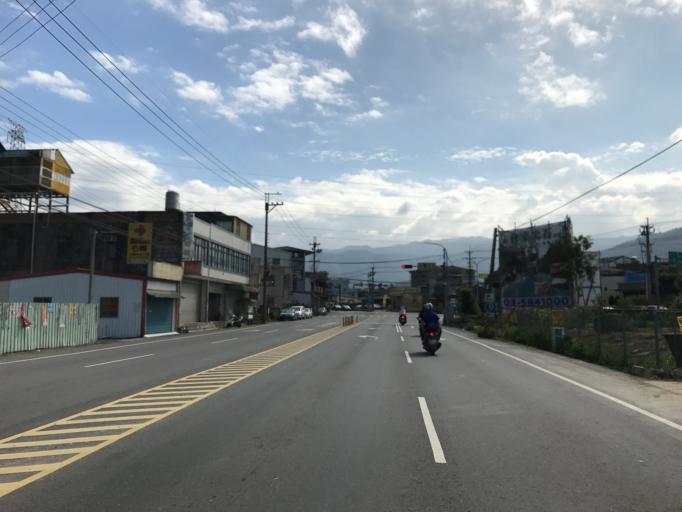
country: TW
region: Taiwan
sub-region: Hsinchu
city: Zhubei
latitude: 24.7271
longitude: 121.1288
